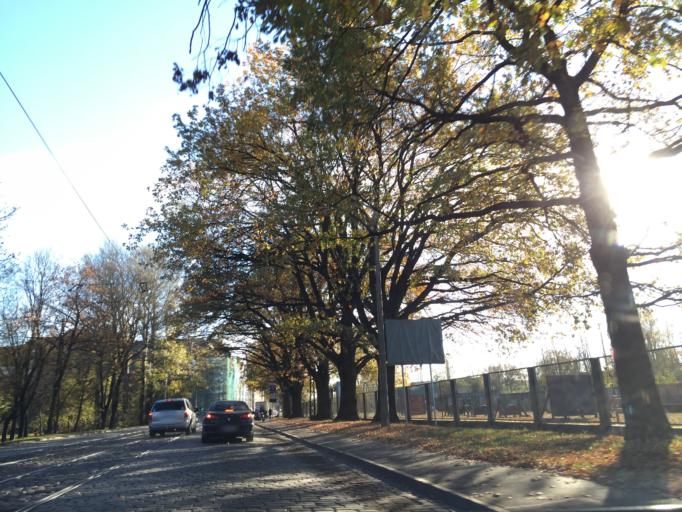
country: LV
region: Riga
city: Riga
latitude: 56.9638
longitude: 24.0980
